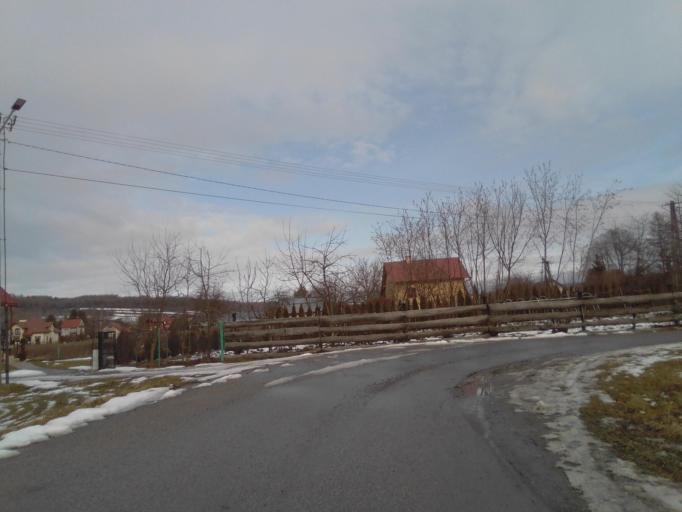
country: PL
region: Subcarpathian Voivodeship
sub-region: Powiat przemyski
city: Nienadowa
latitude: 49.8177
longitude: 22.4161
